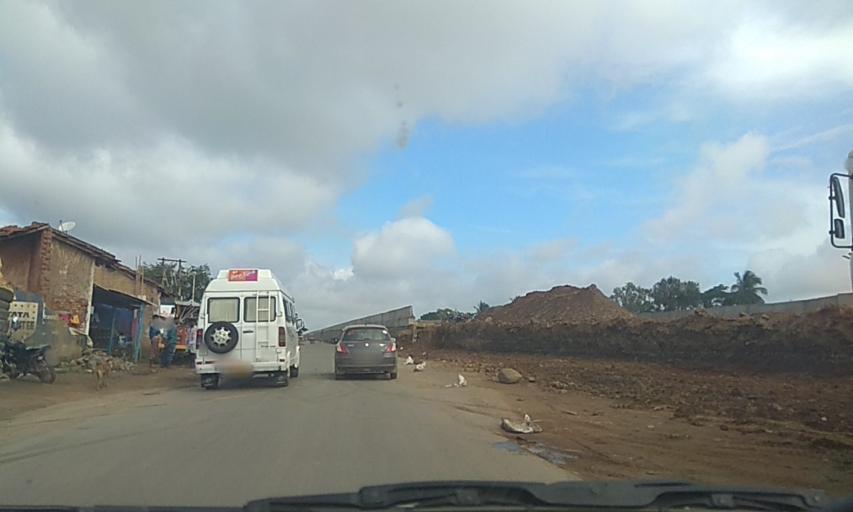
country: IN
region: Karnataka
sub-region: Haveri
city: Shiggaon
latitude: 14.9908
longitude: 75.2175
